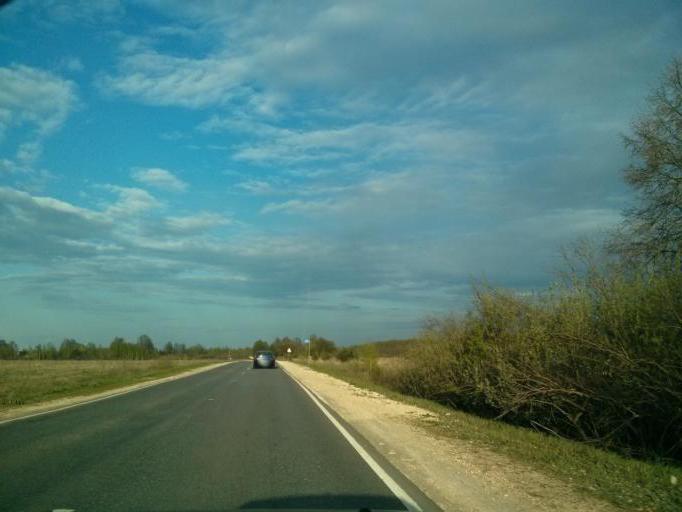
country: RU
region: Nizjnij Novgorod
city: Navashino
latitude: 55.6041
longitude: 42.1863
